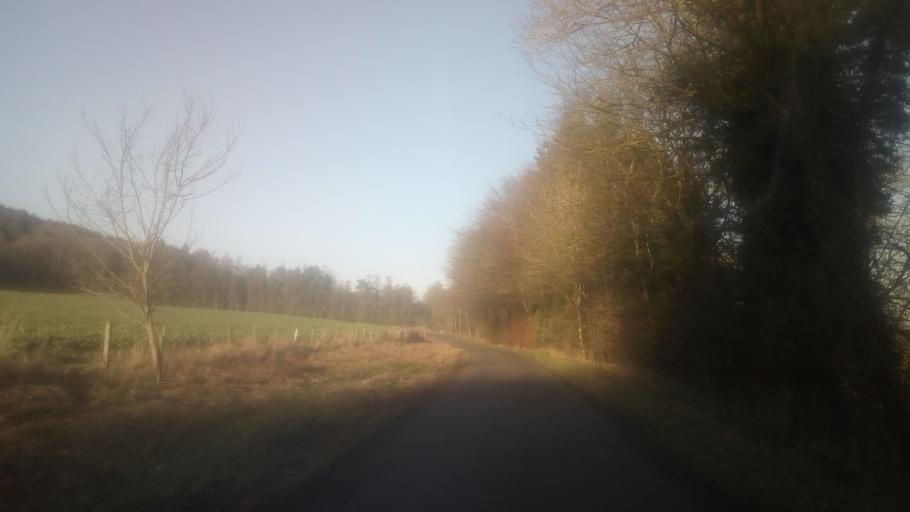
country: GB
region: Scotland
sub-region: The Scottish Borders
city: Saint Boswells
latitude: 55.4758
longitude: -2.6598
